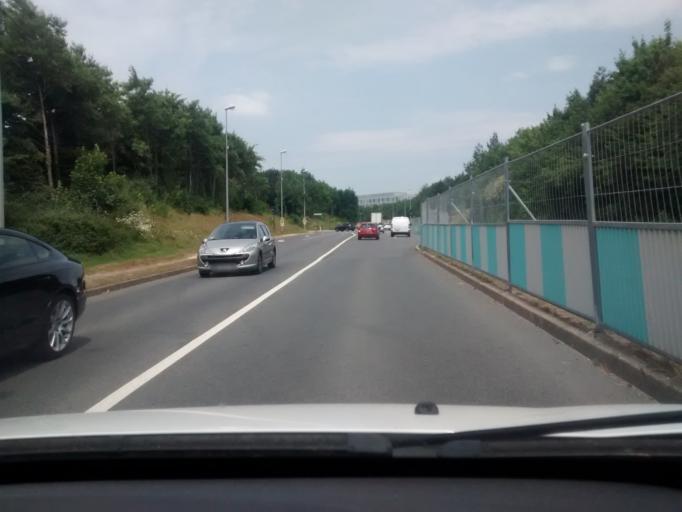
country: FR
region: Brittany
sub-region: Departement d'Ille-et-Vilaine
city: Cesson-Sevigne
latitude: 48.1297
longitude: -1.6211
